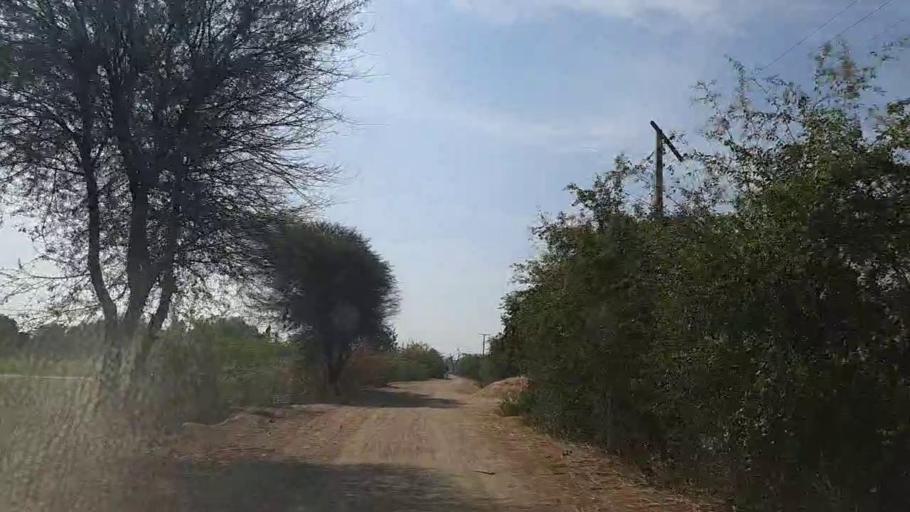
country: PK
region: Sindh
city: Mirpur Khas
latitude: 25.4729
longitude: 68.9745
